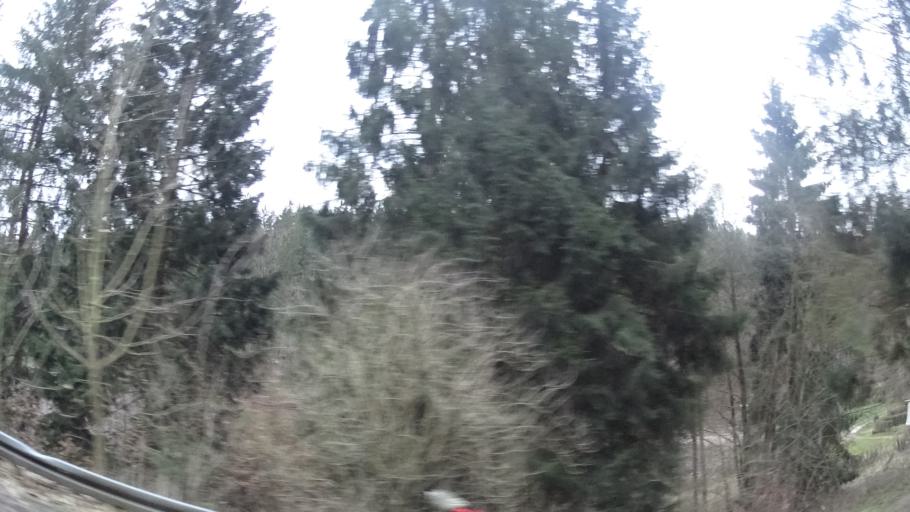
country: DE
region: Thuringia
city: Herschdorf
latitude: 50.7056
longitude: 11.4890
